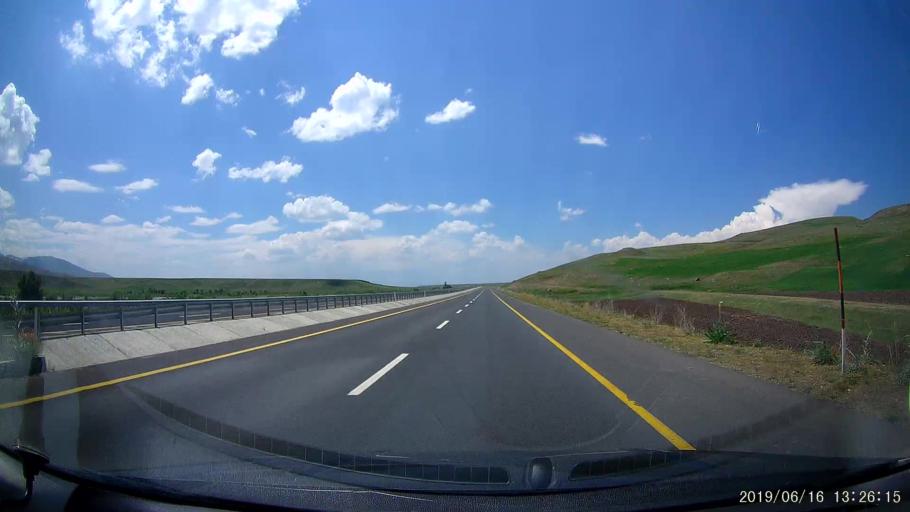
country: TR
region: Agri
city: Taslicay
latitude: 39.6579
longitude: 43.3326
